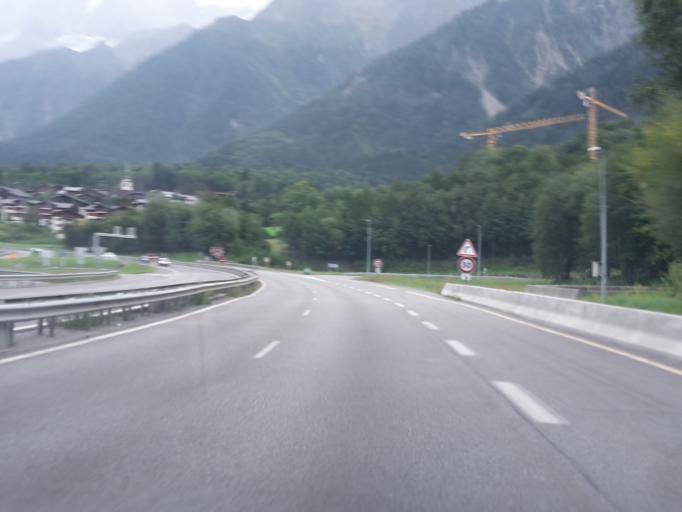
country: FR
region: Rhone-Alpes
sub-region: Departement de la Haute-Savoie
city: Les Houches
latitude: 45.8919
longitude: 6.7907
